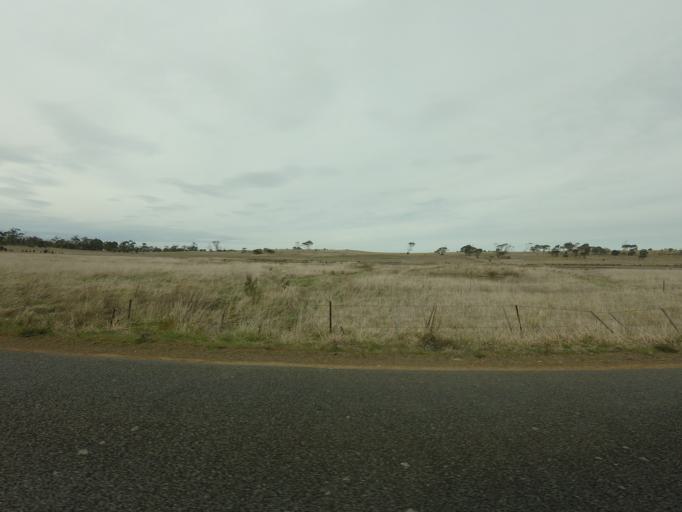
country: AU
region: Tasmania
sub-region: Sorell
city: Sorell
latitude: -42.2748
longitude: 148.0041
